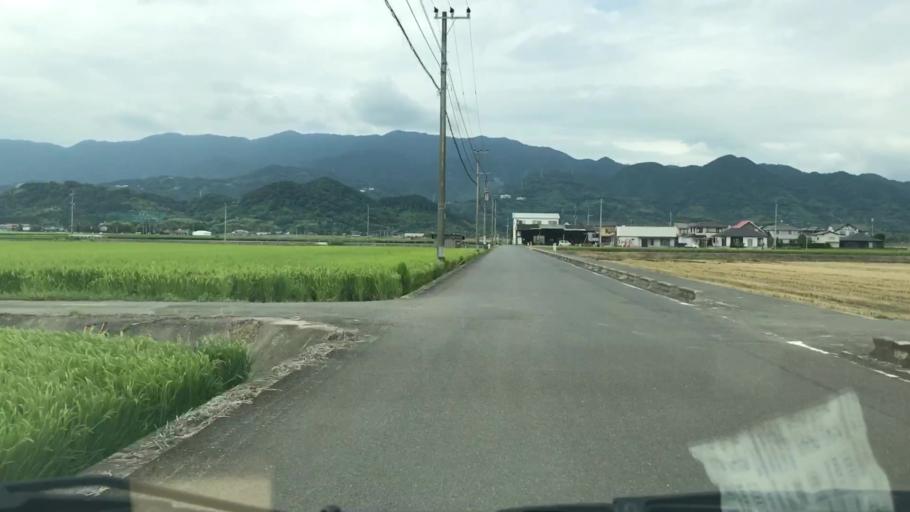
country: JP
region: Saga Prefecture
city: Saga-shi
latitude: 33.2870
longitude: 130.2250
